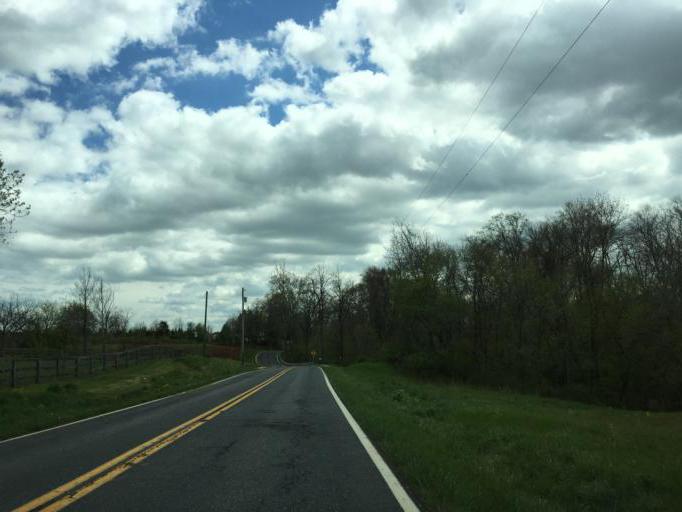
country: US
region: Maryland
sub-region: Frederick County
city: Thurmont
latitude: 39.5758
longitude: -77.3923
